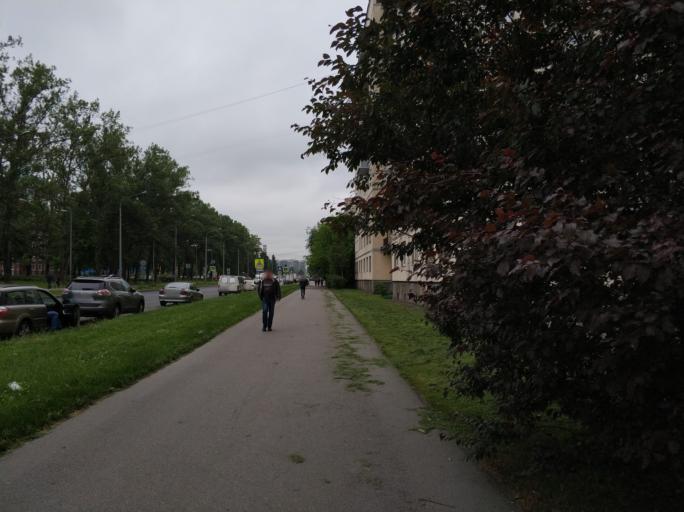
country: RU
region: St.-Petersburg
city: Grazhdanka
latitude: 60.0390
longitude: 30.4131
